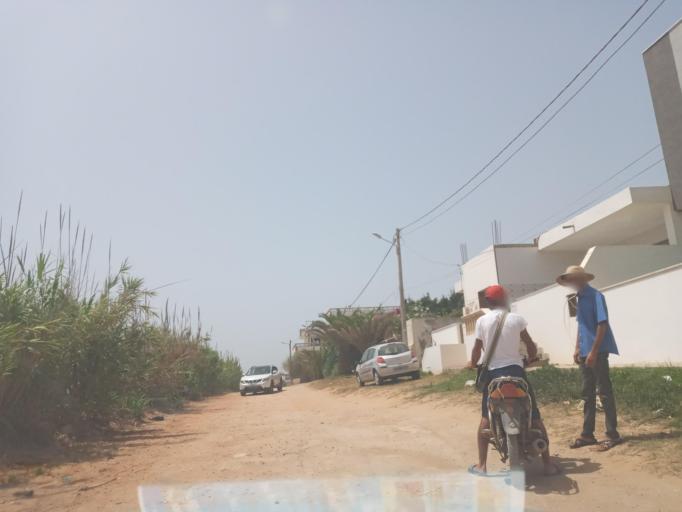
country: TN
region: Nabul
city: El Haouaria
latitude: 37.0319
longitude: 11.0571
